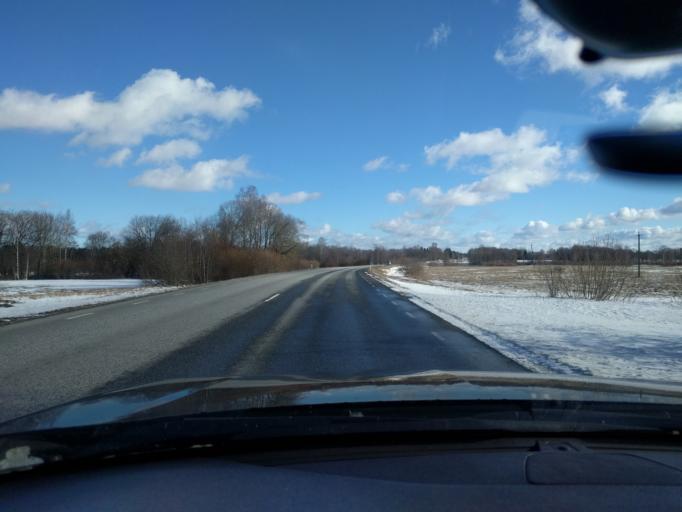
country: EE
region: Harju
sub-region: Raasiku vald
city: Raasiku
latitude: 59.3622
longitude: 25.1615
